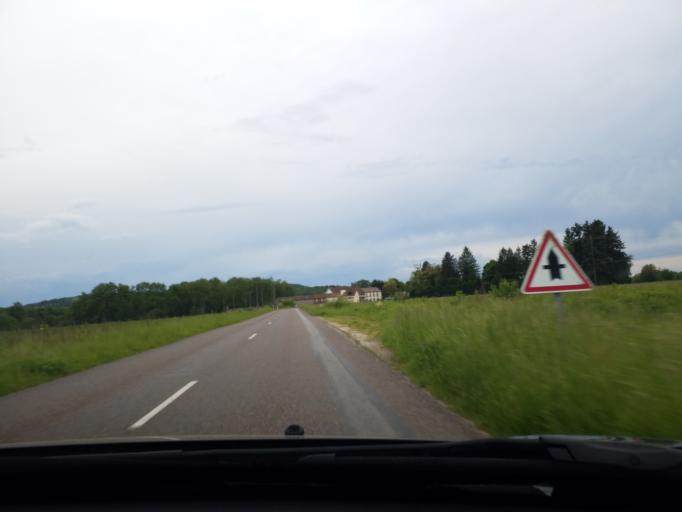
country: FR
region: Franche-Comte
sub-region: Departement de la Haute-Saone
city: Corbenay
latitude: 47.8853
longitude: 6.3142
